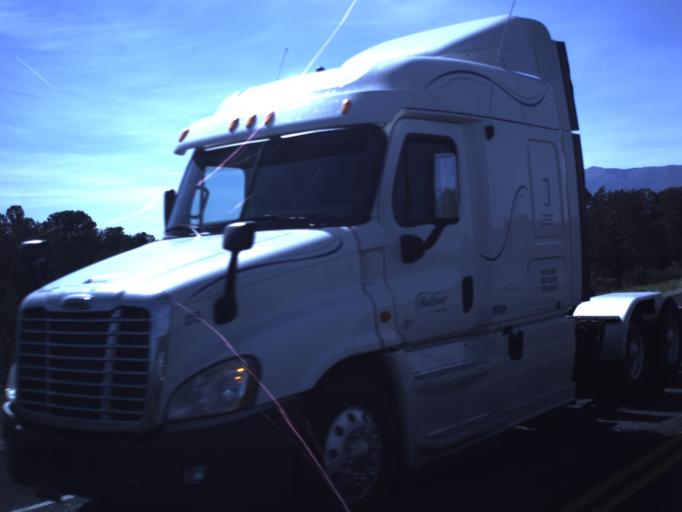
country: US
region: Utah
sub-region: San Juan County
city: Monticello
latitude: 37.8601
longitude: -109.2077
